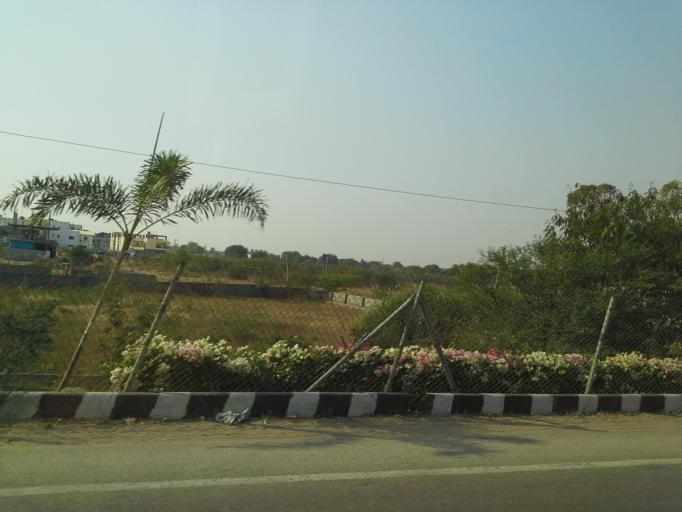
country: IN
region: Telangana
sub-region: Rangareddi
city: Balapur
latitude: 17.2691
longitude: 78.3959
